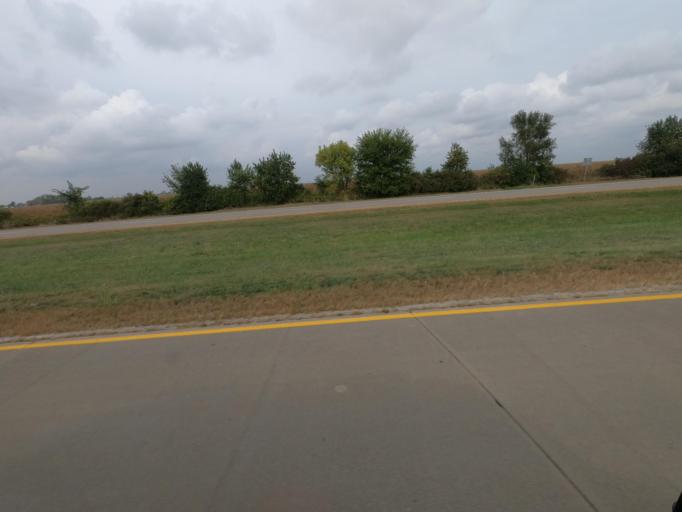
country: US
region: Iowa
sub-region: Wapello County
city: Ottumwa
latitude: 41.0921
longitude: -92.4220
